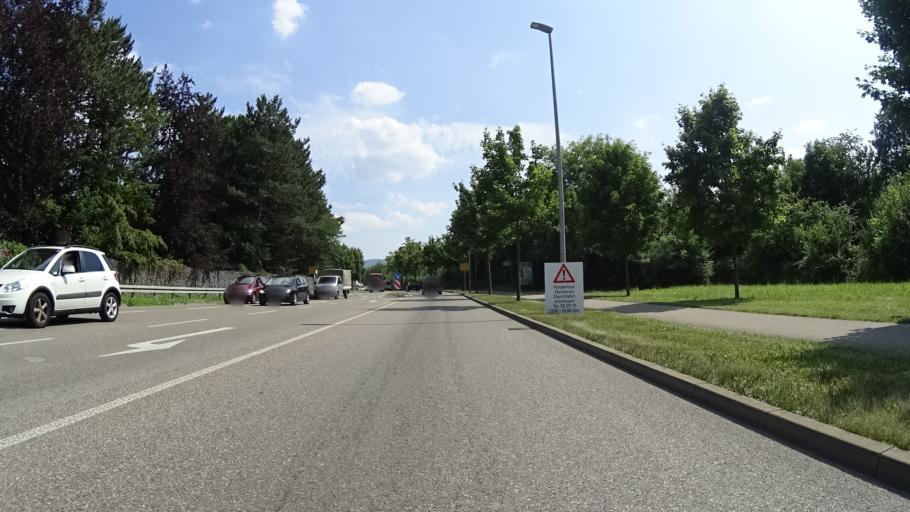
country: DE
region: Baden-Wuerttemberg
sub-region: Regierungsbezirk Stuttgart
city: Eislingen
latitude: 48.6909
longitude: 9.6822
